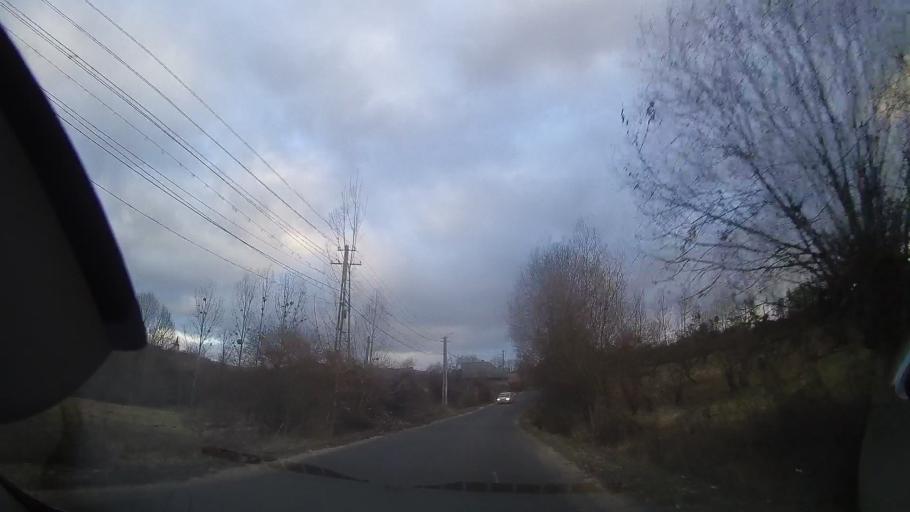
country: RO
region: Cluj
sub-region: Comuna Calatele
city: Calatele
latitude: 46.7829
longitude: 23.0215
